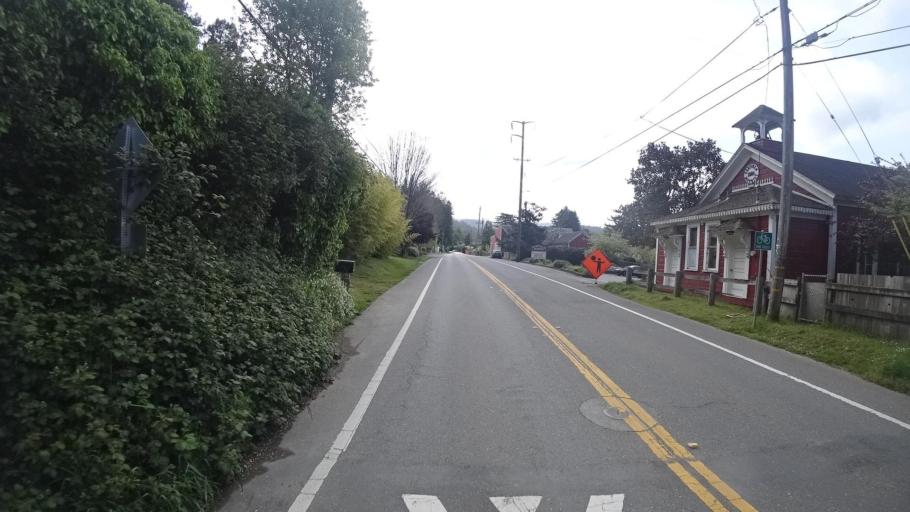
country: US
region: California
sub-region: Humboldt County
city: Myrtletown
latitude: 40.7617
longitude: -124.0617
